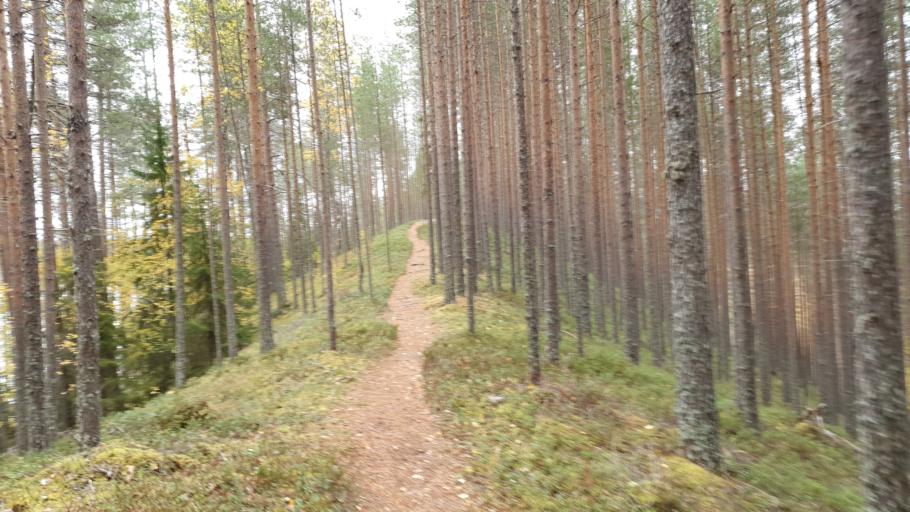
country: FI
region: Kainuu
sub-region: Kehys-Kainuu
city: Kuhmo
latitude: 64.2933
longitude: 29.3468
